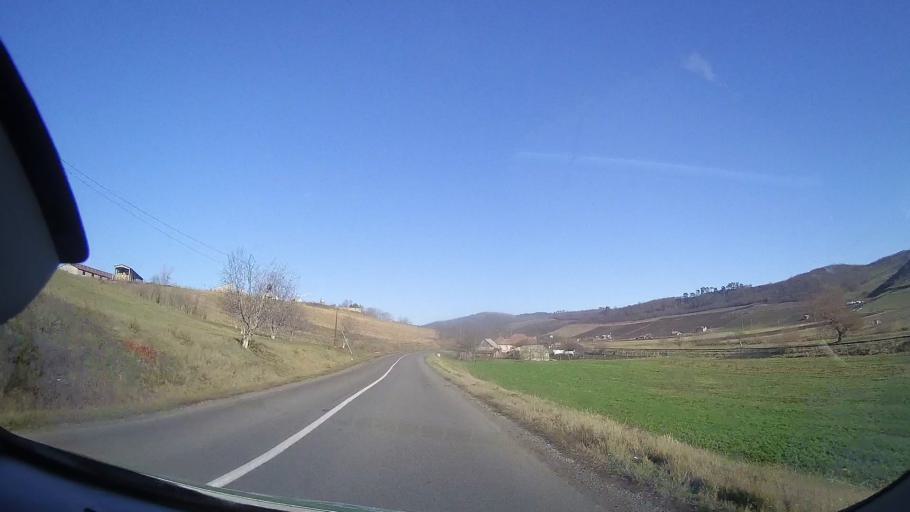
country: RO
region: Mures
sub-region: Comuna Sarmasu
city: Sarmasu
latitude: 46.7731
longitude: 24.1980
